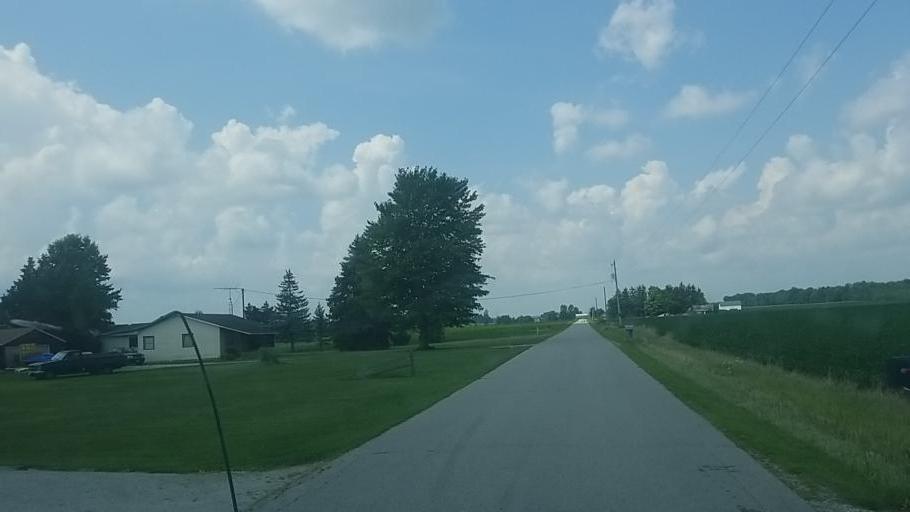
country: US
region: Ohio
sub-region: Crawford County
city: Galion
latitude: 40.7993
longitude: -82.8461
